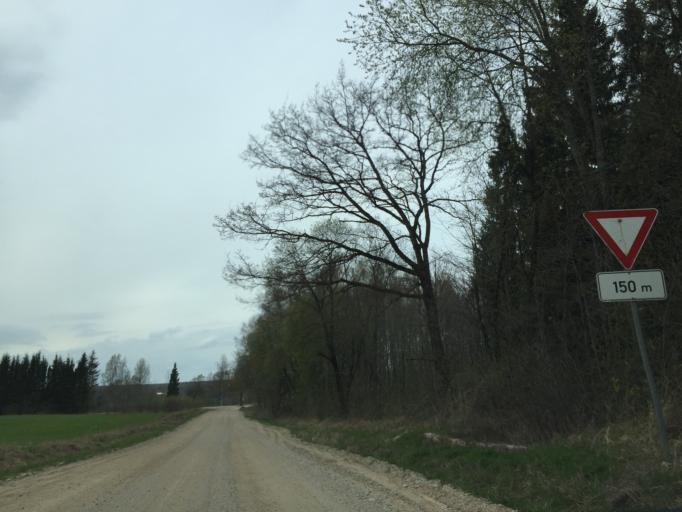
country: LV
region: Priekuli
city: Priekuli
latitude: 57.3445
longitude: 25.3462
